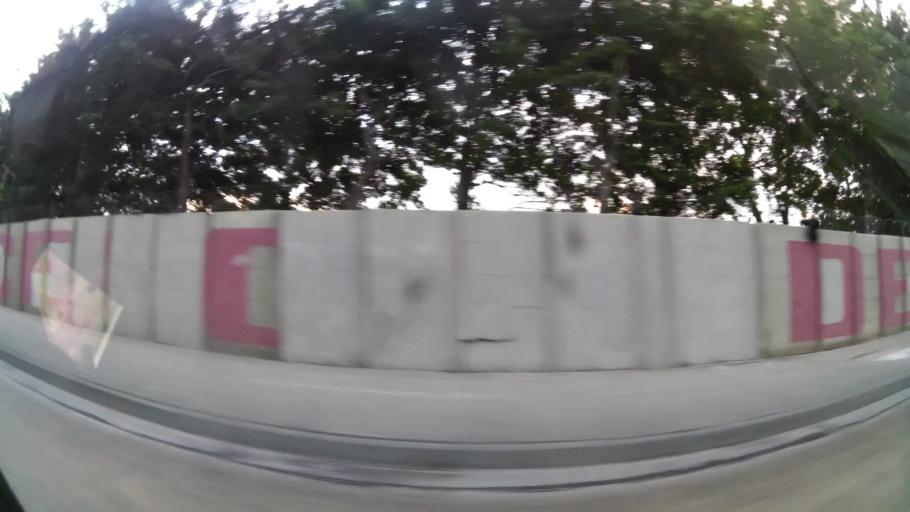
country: EC
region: Guayas
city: Eloy Alfaro
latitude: -2.1785
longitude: -79.8830
